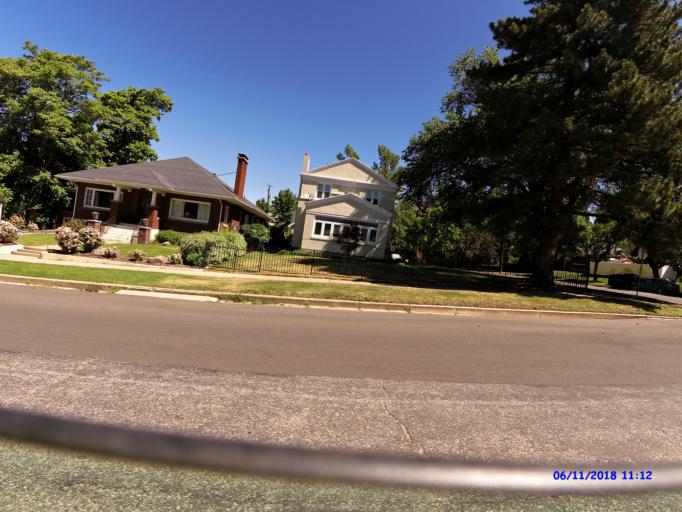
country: US
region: Utah
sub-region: Weber County
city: Ogden
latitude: 41.2202
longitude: -111.9407
